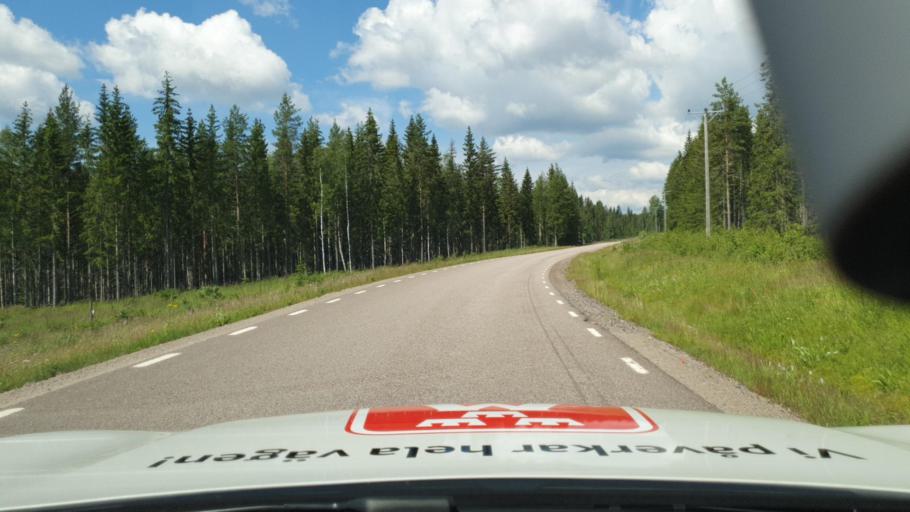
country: SE
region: Vaermland
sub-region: Torsby Kommun
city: Torsby
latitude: 60.4541
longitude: 12.8878
